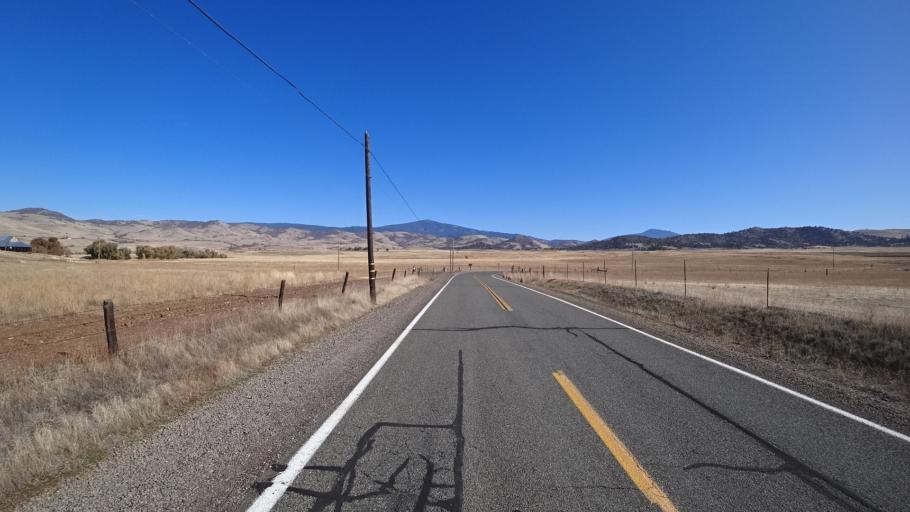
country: US
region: California
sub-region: Siskiyou County
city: Montague
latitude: 41.8081
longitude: -122.4173
